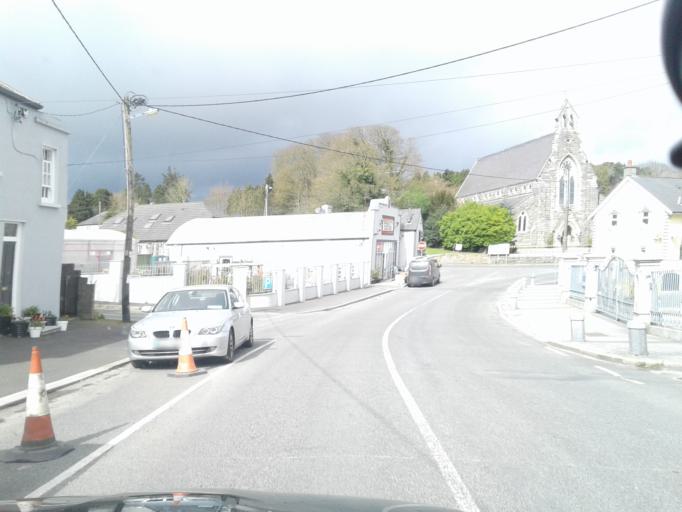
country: IE
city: Newtownmountkennedy
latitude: 53.0616
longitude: -6.2244
